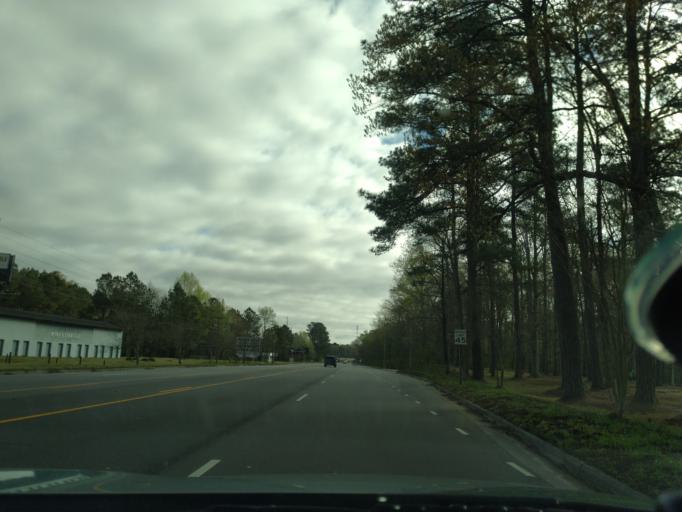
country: US
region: North Carolina
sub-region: Washington County
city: Plymouth
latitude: 35.8653
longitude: -76.7264
